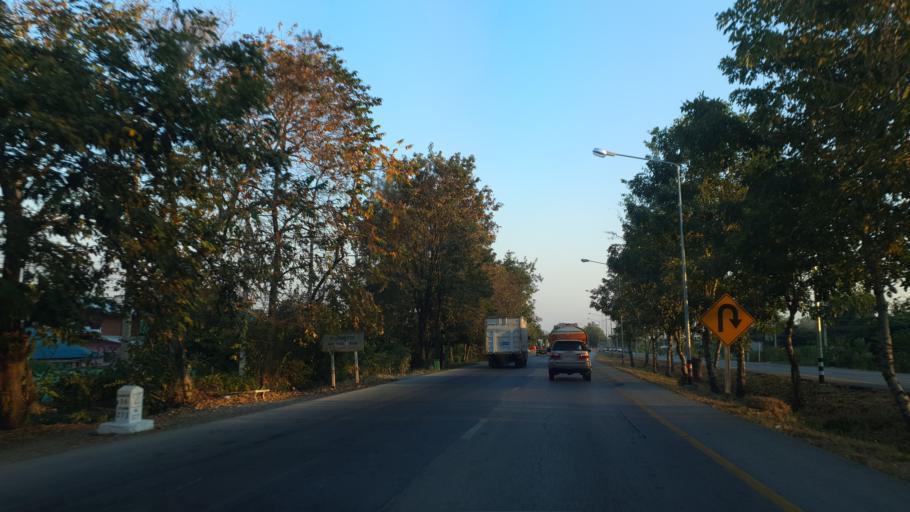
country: TH
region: Nakhon Sawan
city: Banphot Phisai
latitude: 15.9095
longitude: 99.8885
